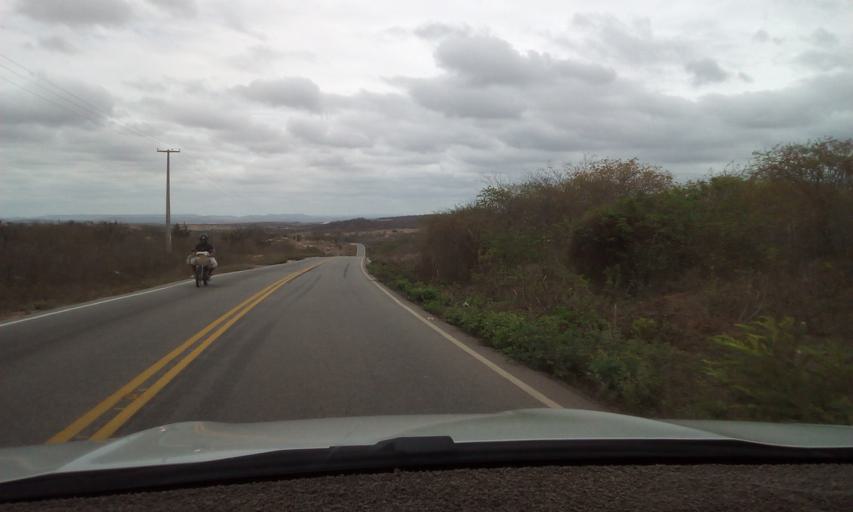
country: BR
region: Paraiba
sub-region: Picui
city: Picui
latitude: -6.5706
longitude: -36.2727
